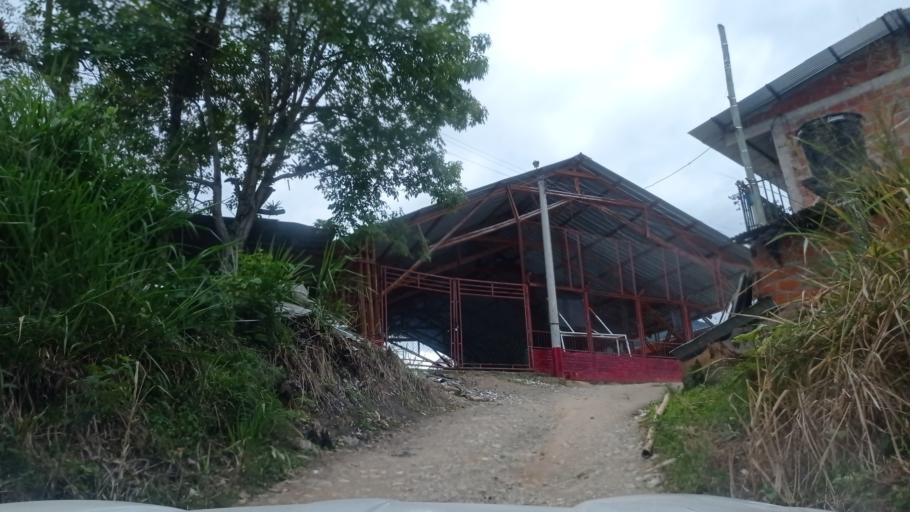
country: CO
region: Huila
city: Garzon
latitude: 2.1032
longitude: -75.6301
